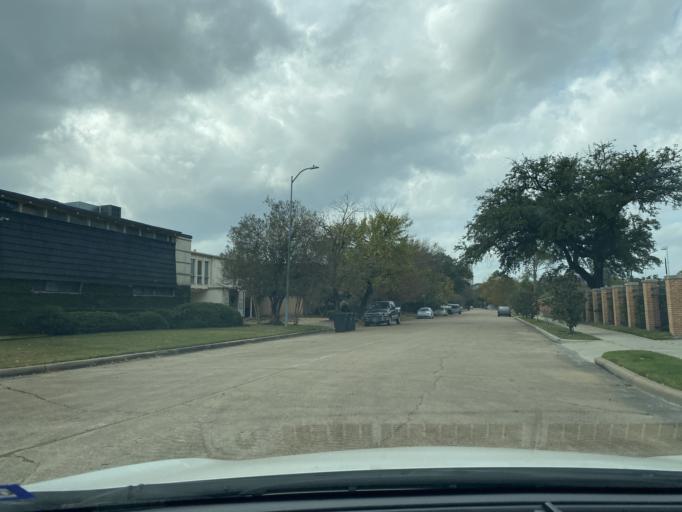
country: US
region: Texas
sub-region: Harris County
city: Hunters Creek Village
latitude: 29.7469
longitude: -95.4645
